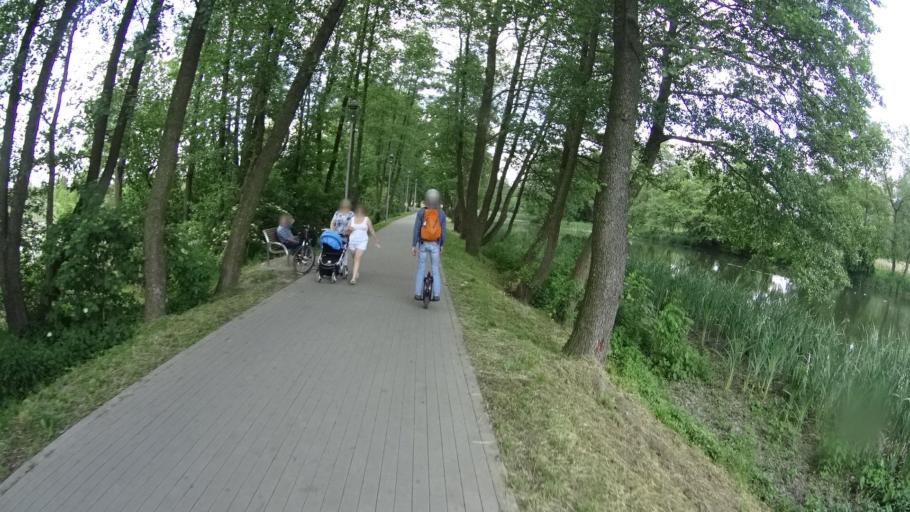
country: PL
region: Masovian Voivodeship
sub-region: Powiat piaseczynski
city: Konstancin-Jeziorna
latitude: 52.0886
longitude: 21.1169
